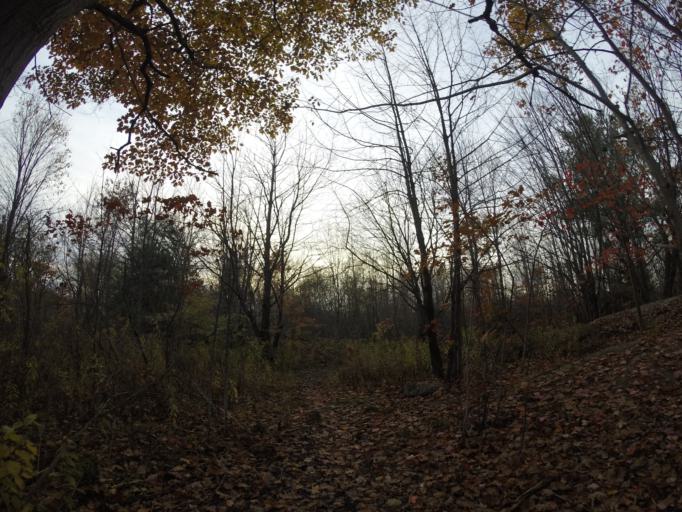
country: CA
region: Ontario
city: Espanola
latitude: 45.9707
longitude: -81.5051
